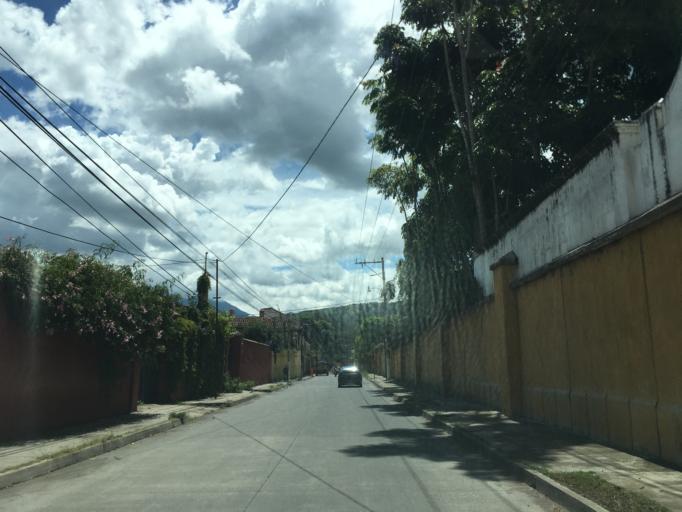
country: GT
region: Sacatepequez
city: Antigua Guatemala
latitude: 14.5437
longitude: -90.7441
